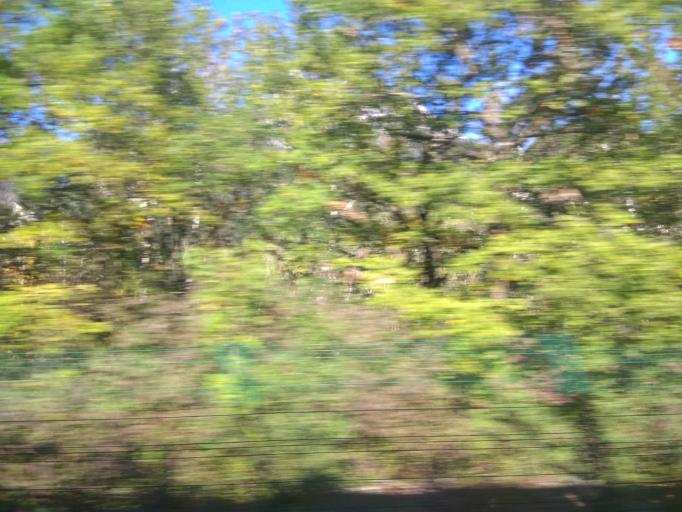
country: FR
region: Rhone-Alpes
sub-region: Departement de la Haute-Savoie
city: Domancy
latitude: 45.9223
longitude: 6.6571
